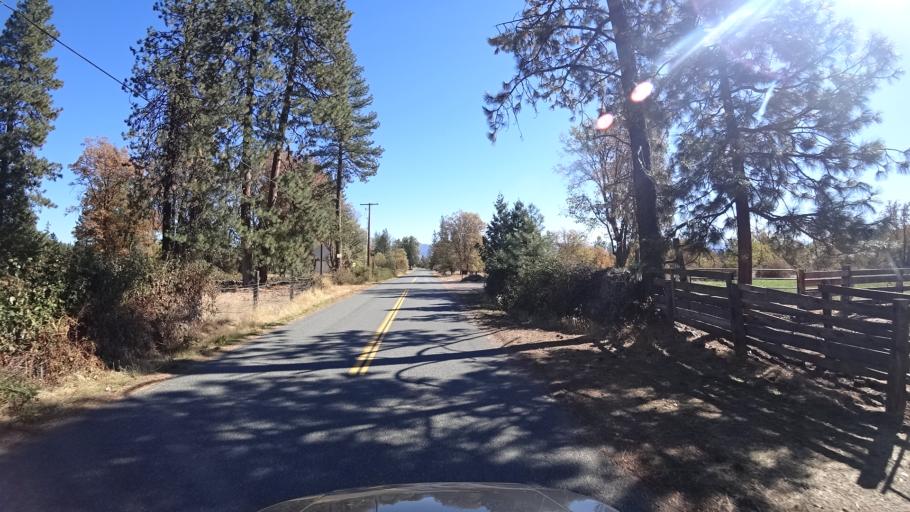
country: US
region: California
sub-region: Siskiyou County
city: Yreka
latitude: 41.5380
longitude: -122.9265
